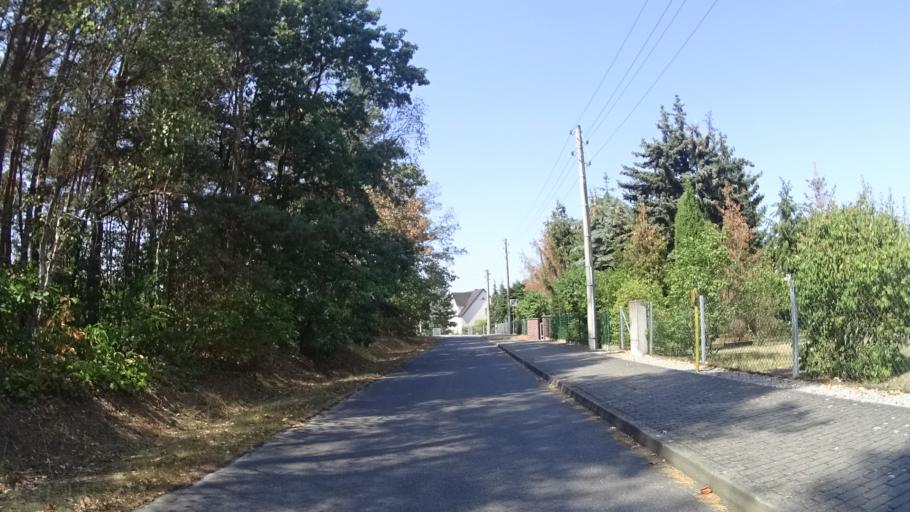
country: DE
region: Brandenburg
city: Tschernitz
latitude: 51.6015
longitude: 14.5877
